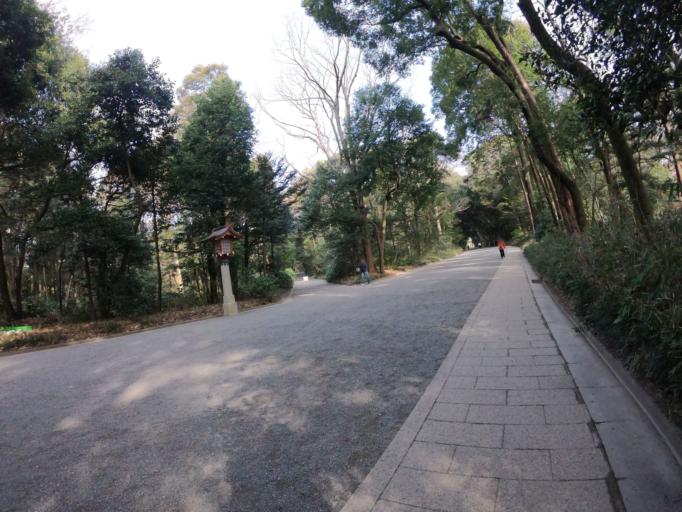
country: JP
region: Chiba
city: Ichihara
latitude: 35.4610
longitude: 140.0168
